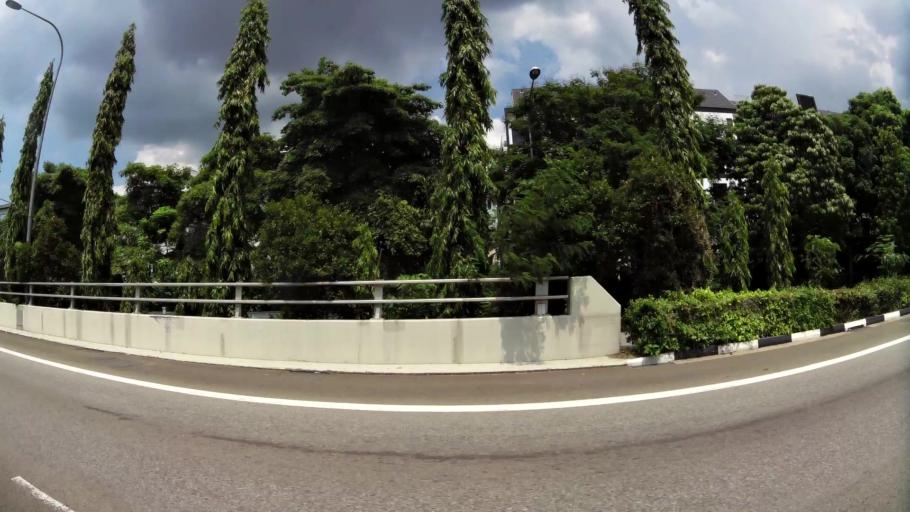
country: SG
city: Singapore
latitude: 1.2907
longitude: 103.7696
